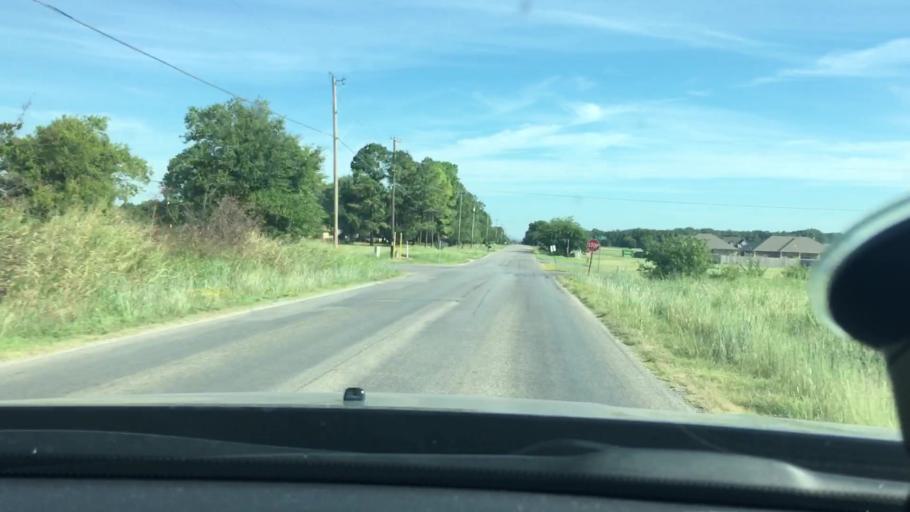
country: US
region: Oklahoma
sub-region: Carter County
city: Lone Grove
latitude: 34.2014
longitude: -97.2475
